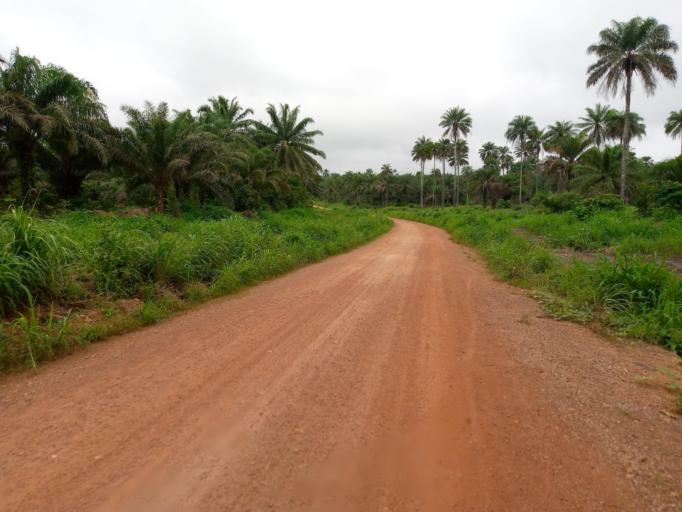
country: SL
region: Southern Province
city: Sumbuya
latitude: 7.5719
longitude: -12.0886
